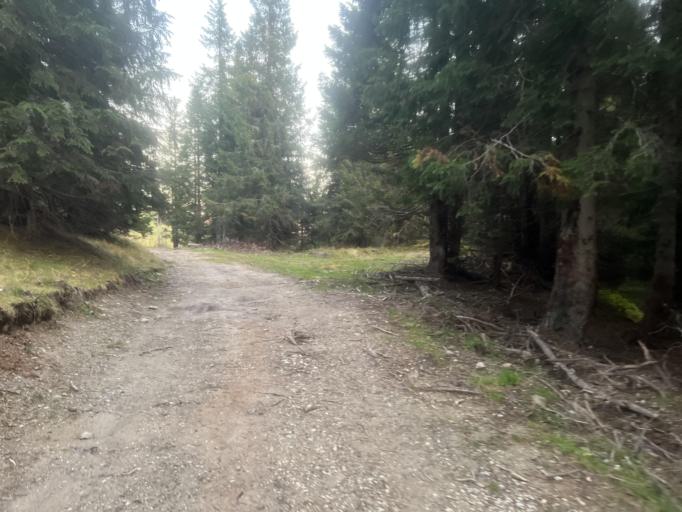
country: IT
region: Veneto
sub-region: Provincia di Belluno
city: Granvilla
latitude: 46.6236
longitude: 12.7062
